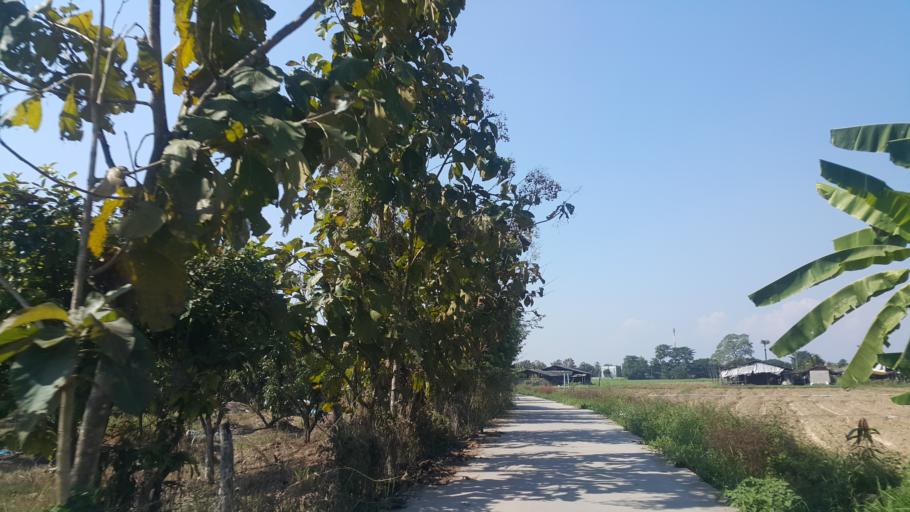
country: TH
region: Chiang Mai
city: San Kamphaeng
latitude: 18.6912
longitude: 99.1656
